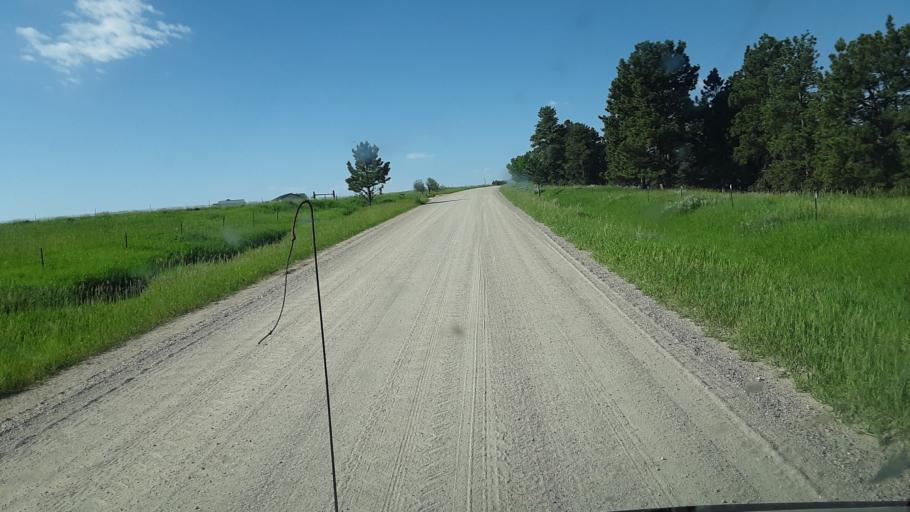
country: US
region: Montana
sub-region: Carbon County
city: Red Lodge
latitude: 45.3567
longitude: -109.1590
